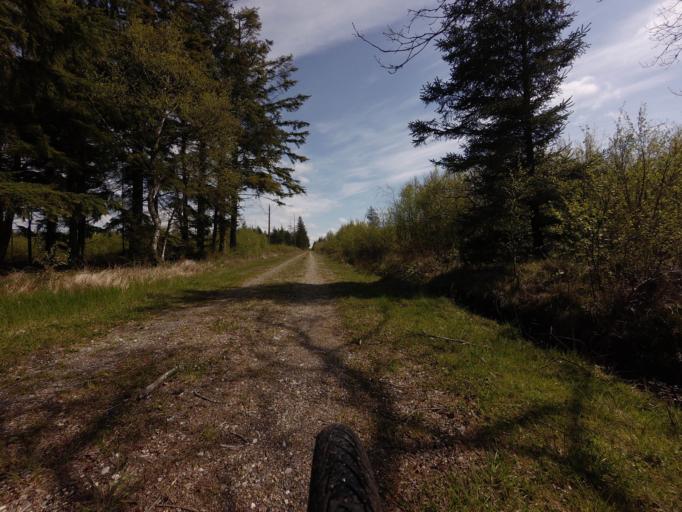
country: DK
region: North Denmark
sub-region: Jammerbugt Kommune
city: Brovst
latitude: 57.1691
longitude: 9.5442
